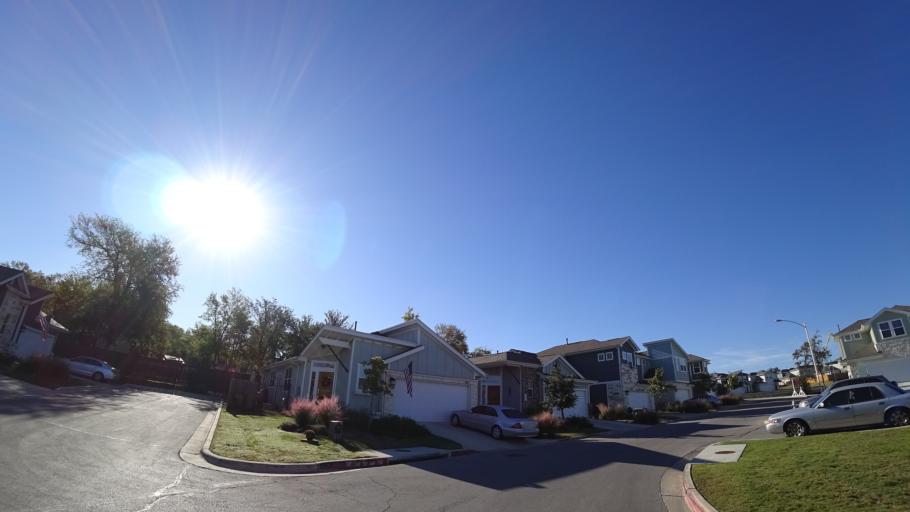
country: US
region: Texas
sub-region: Travis County
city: Austin
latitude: 30.2189
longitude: -97.6985
